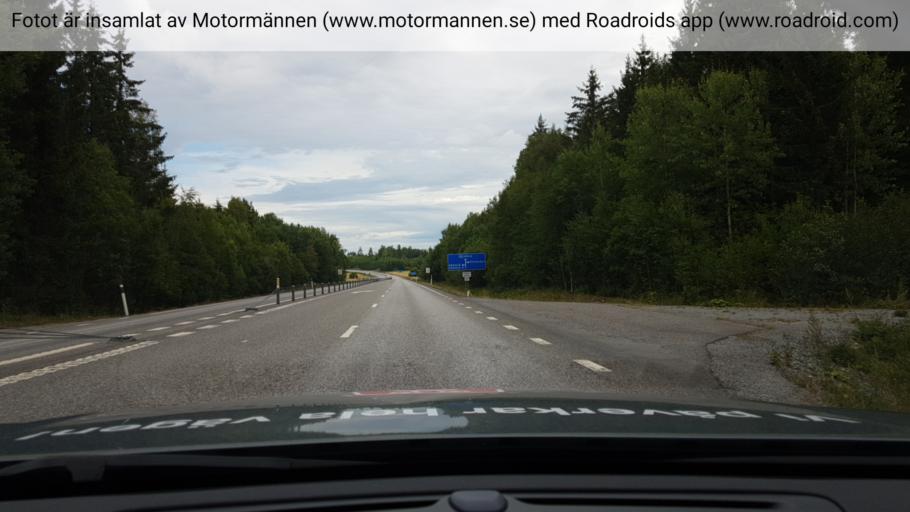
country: SE
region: Uppsala
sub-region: Heby Kommun
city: Tarnsjo
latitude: 60.1615
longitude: 16.9525
